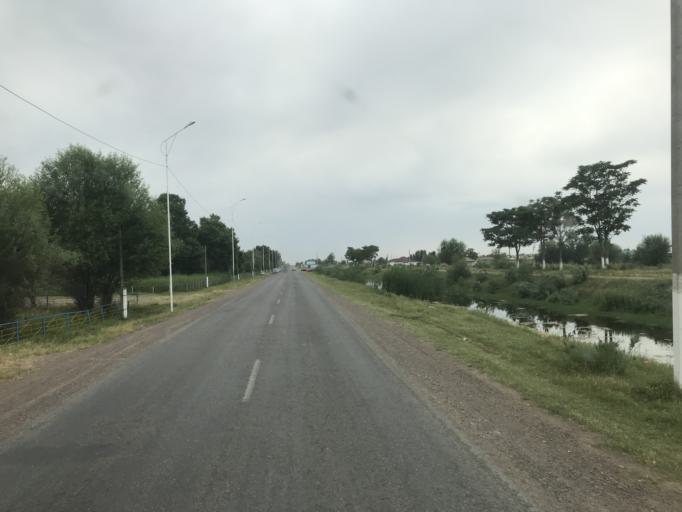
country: KZ
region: Ongtustik Qazaqstan
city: Asykata
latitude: 40.9373
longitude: 68.4117
